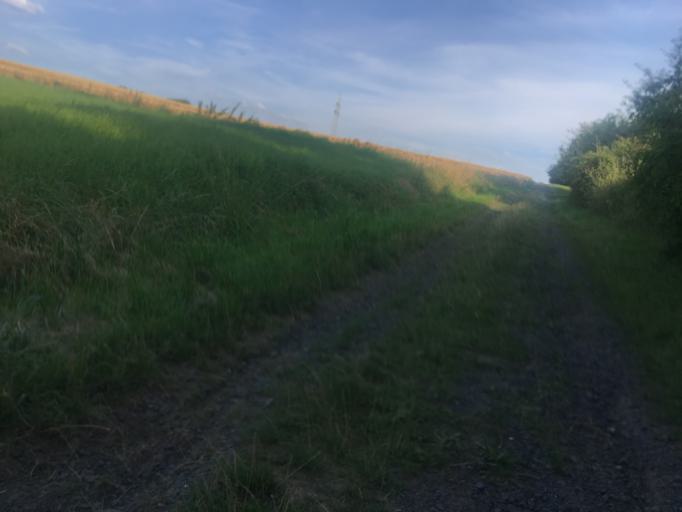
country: DE
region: Hesse
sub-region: Regierungsbezirk Darmstadt
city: Gelnhausen
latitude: 50.1802
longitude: 9.1653
